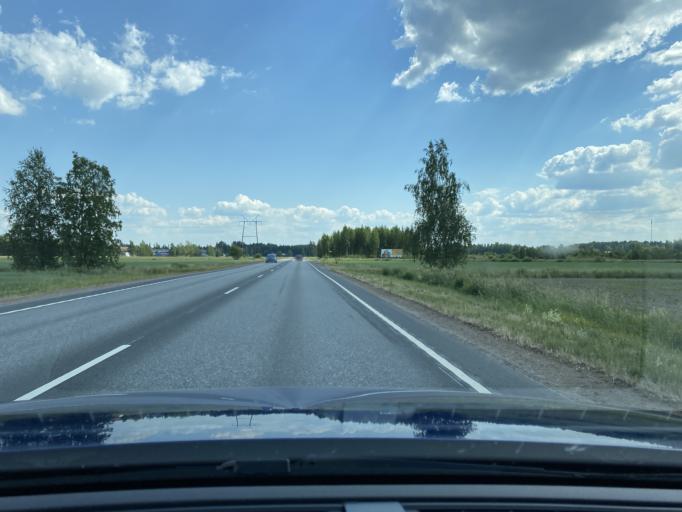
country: FI
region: Satakunta
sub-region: Rauma
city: Eura
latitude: 61.1426
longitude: 22.1104
